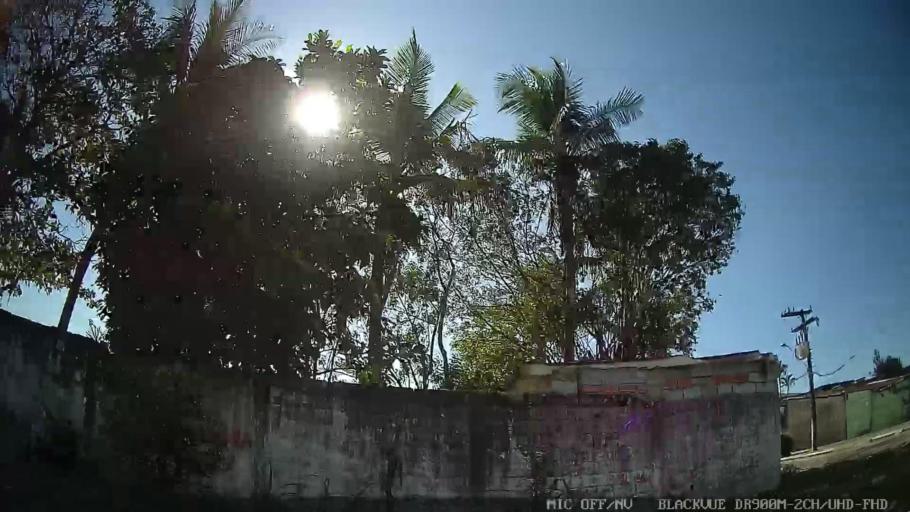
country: BR
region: Sao Paulo
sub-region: Guaruja
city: Guaruja
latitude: -23.9641
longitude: -46.2746
